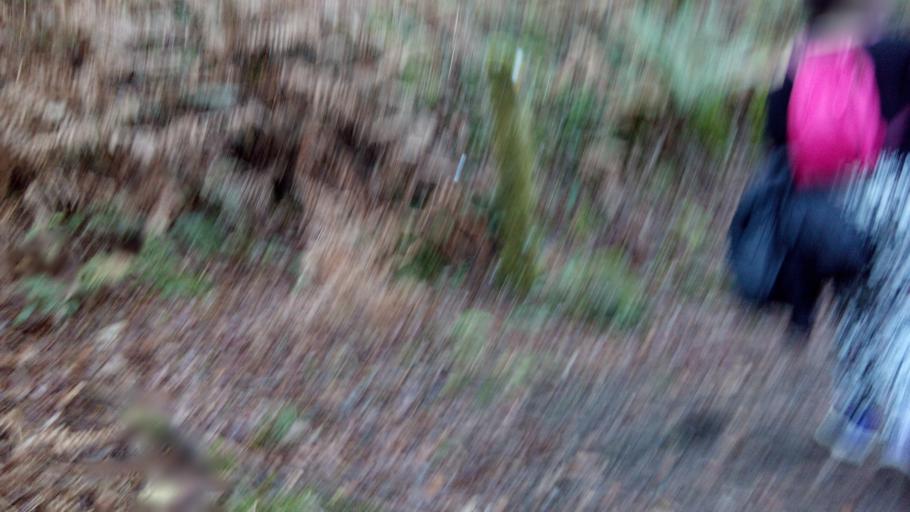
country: ES
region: Galicia
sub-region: Provincia de Pontevedra
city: Meis
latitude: 42.4751
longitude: -8.7433
